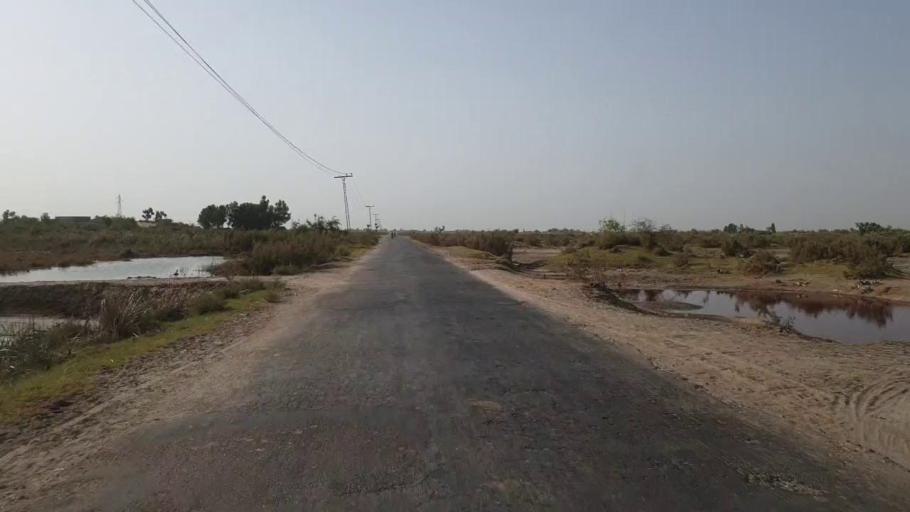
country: PK
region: Sindh
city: Khadro
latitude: 26.3443
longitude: 68.9250
